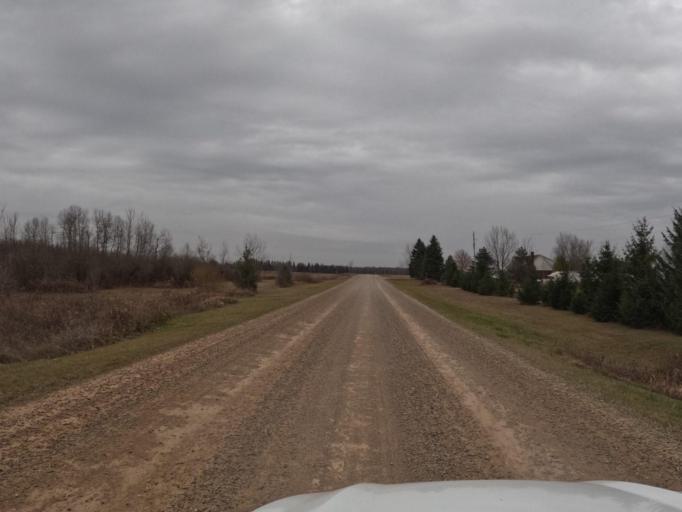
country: CA
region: Ontario
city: Shelburne
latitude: 43.8724
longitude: -80.3560
